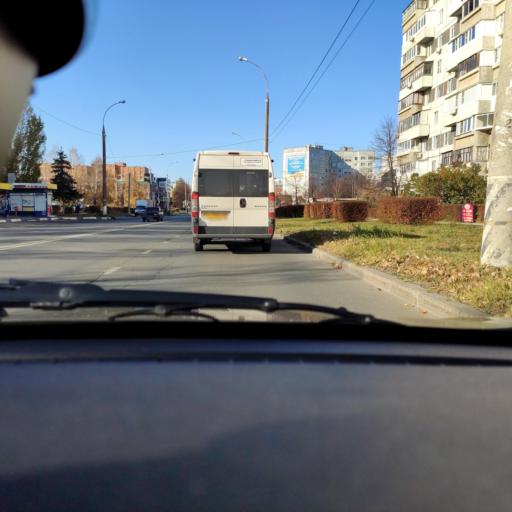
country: RU
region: Samara
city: Tol'yatti
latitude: 53.5335
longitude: 49.3309
